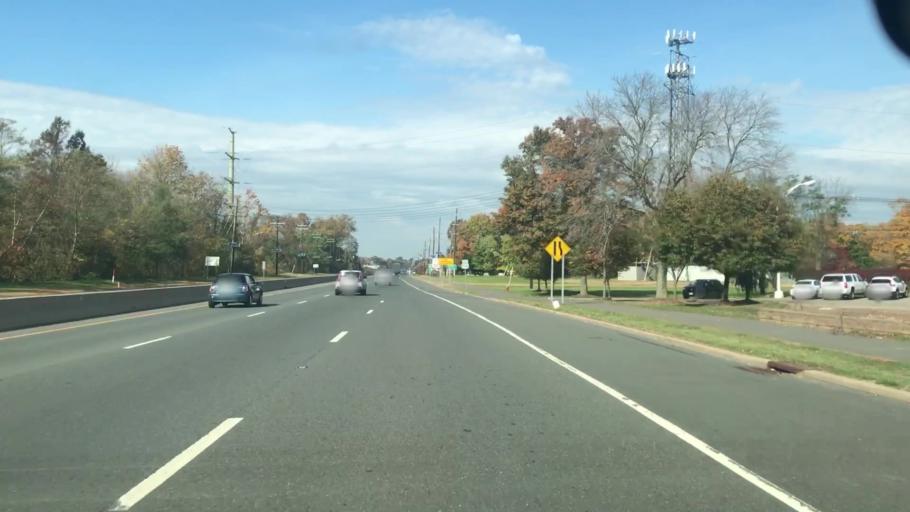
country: US
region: New Jersey
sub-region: Somerset County
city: Somerville
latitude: 40.5583
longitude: -74.6170
